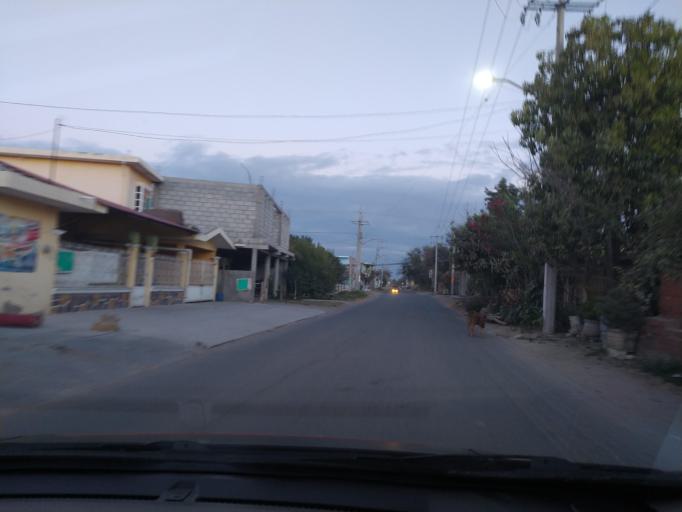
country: LA
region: Oudomxai
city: Muang La
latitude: 21.0100
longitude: 101.8118
